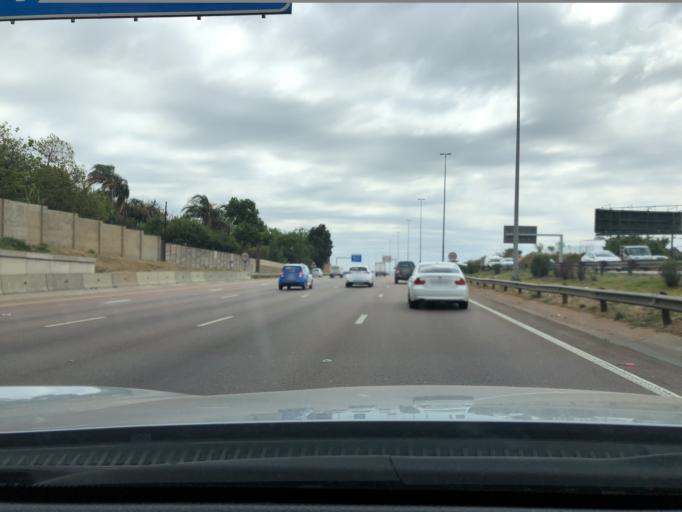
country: ZA
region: Gauteng
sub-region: City of Tshwane Metropolitan Municipality
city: Centurion
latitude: -25.8182
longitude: 28.2541
